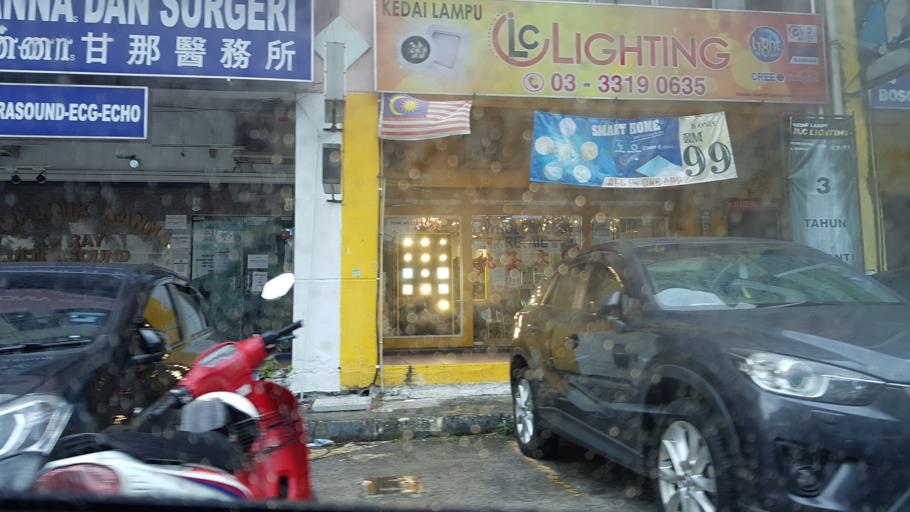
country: MY
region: Selangor
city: Klang
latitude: 3.0076
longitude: 101.4384
